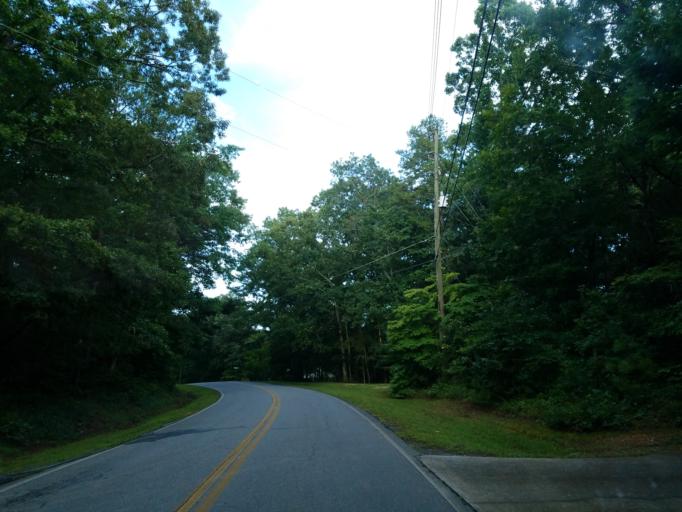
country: US
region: Georgia
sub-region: Bartow County
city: Emerson
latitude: 34.0944
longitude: -84.7553
